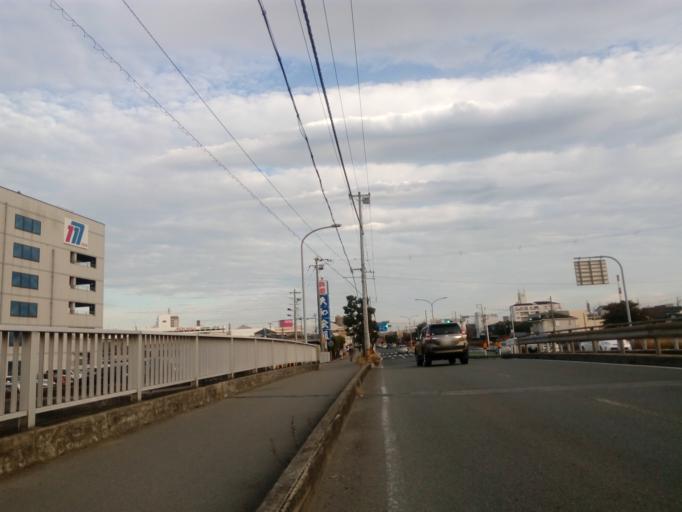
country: JP
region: Hyogo
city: Himeji
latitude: 34.7980
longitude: 134.6633
